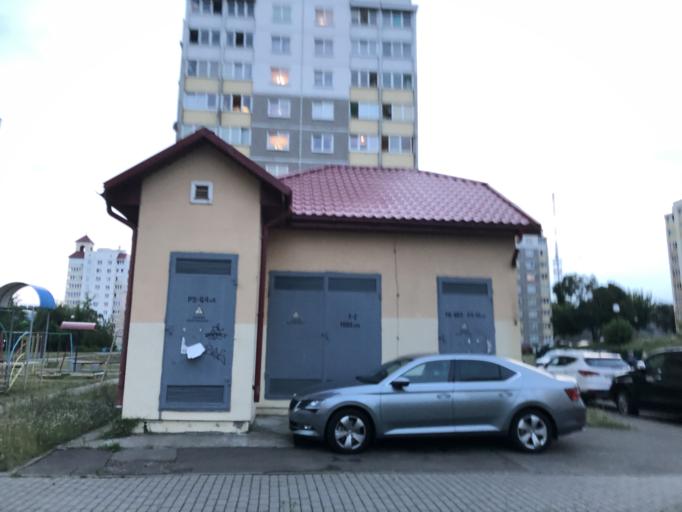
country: BY
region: Grodnenskaya
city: Hrodna
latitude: 53.6980
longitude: 23.8343
